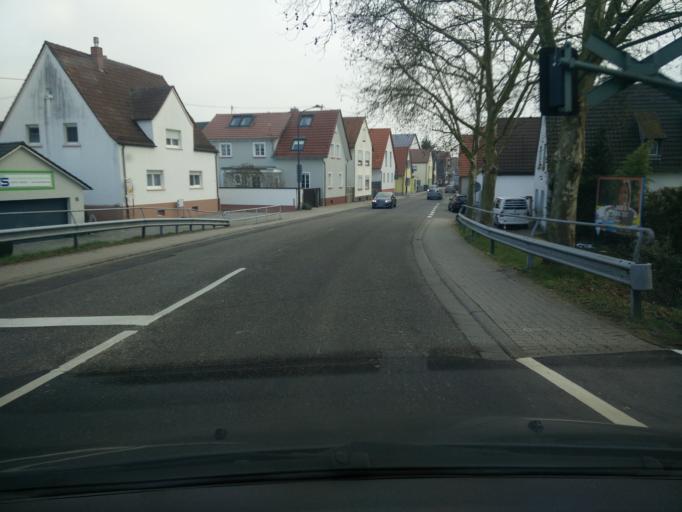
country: DE
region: Rheinland-Pfalz
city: Kandel
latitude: 49.0803
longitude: 8.1881
